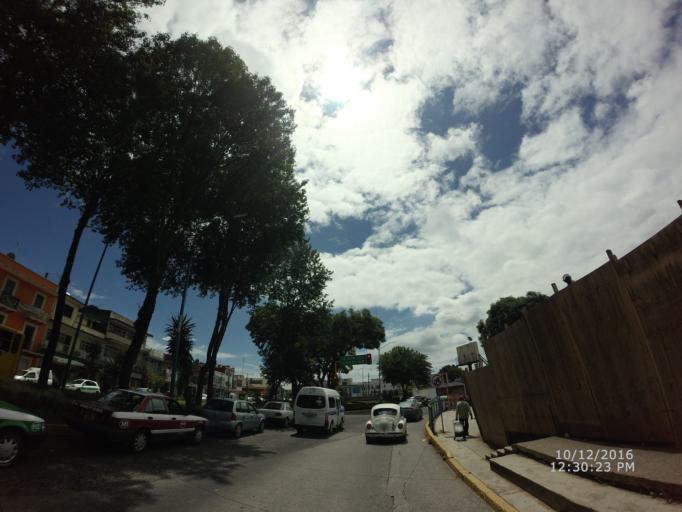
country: MX
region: Veracruz
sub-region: Xalapa
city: Xalapa de Enriquez
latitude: 19.5410
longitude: -96.9263
